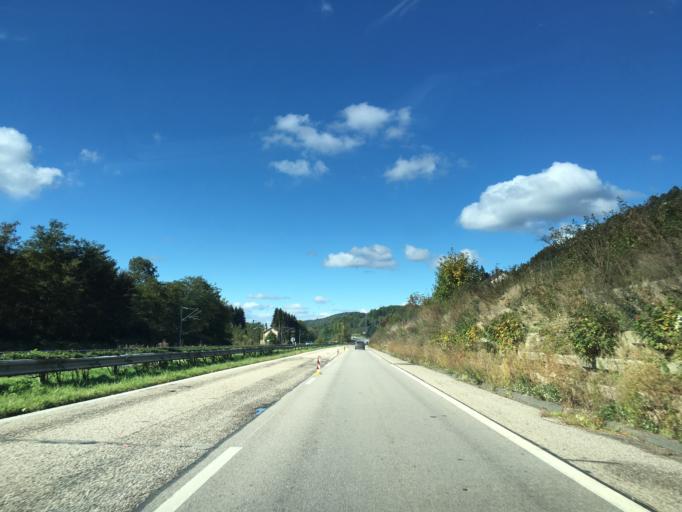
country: FR
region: Lorraine
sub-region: Departement des Vosges
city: Etival-Clairefontaine
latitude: 48.3850
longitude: 6.8678
